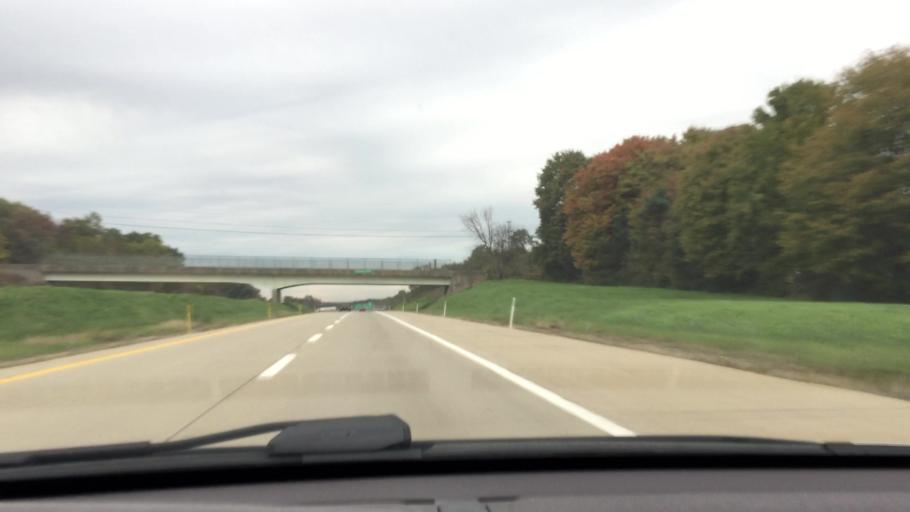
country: US
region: Pennsylvania
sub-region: Beaver County
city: Big Beaver
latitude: 40.8294
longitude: -80.3706
